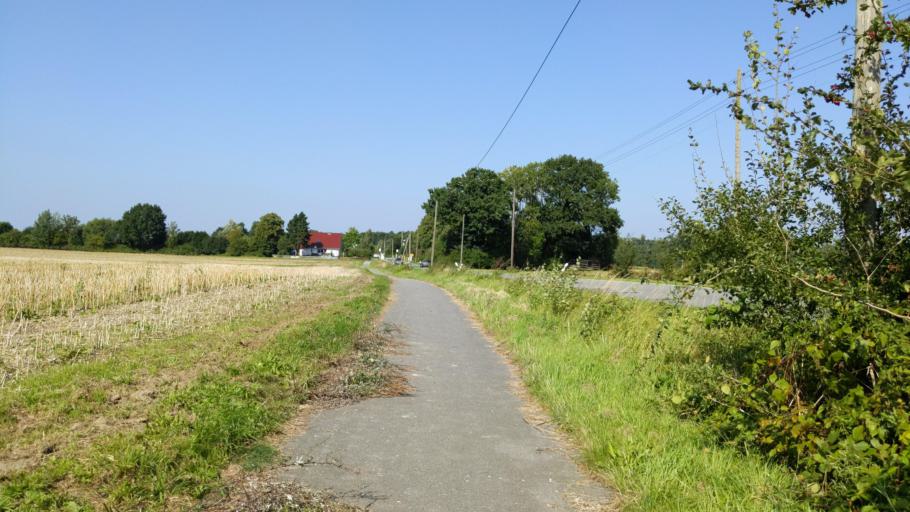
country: DE
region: Schleswig-Holstein
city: Klein Wesenberg
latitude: 53.8044
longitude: 10.5483
